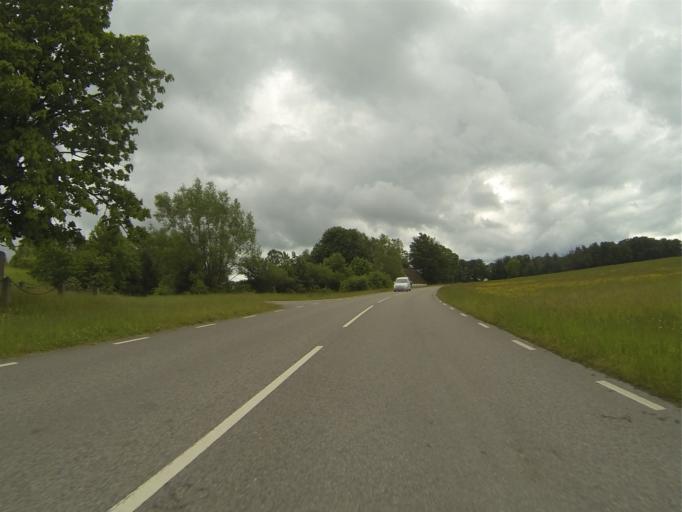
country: SE
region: Skane
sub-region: Lunds Kommun
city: Veberod
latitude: 55.6972
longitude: 13.4228
